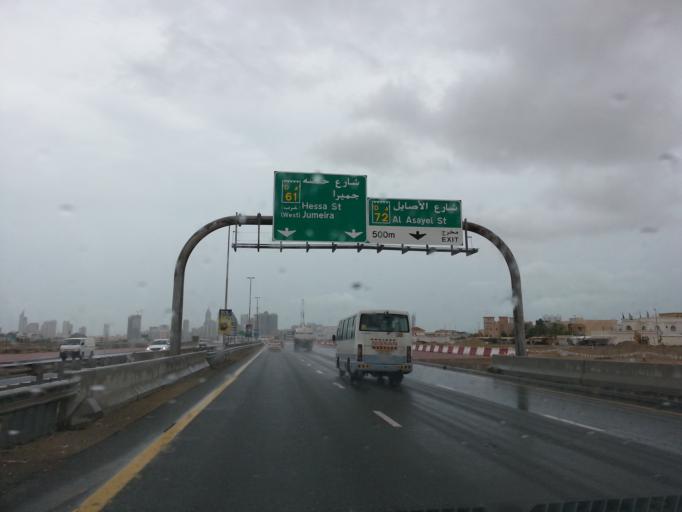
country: AE
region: Dubai
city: Dubai
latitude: 25.0803
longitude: 55.2057
